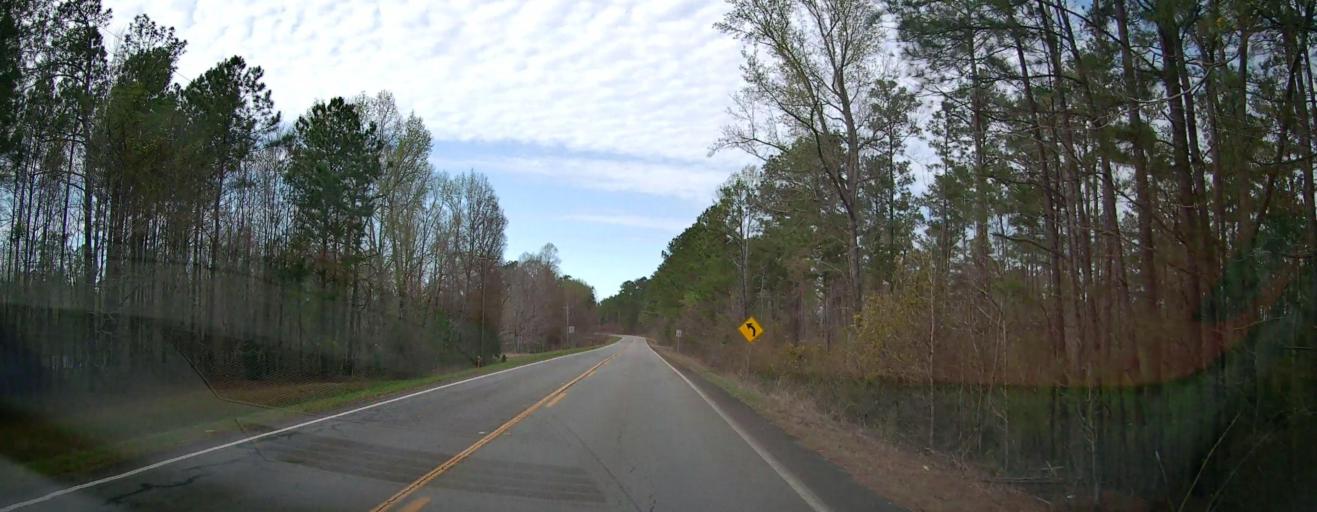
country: US
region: Georgia
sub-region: Jones County
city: Gray
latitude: 32.9908
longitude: -83.6852
